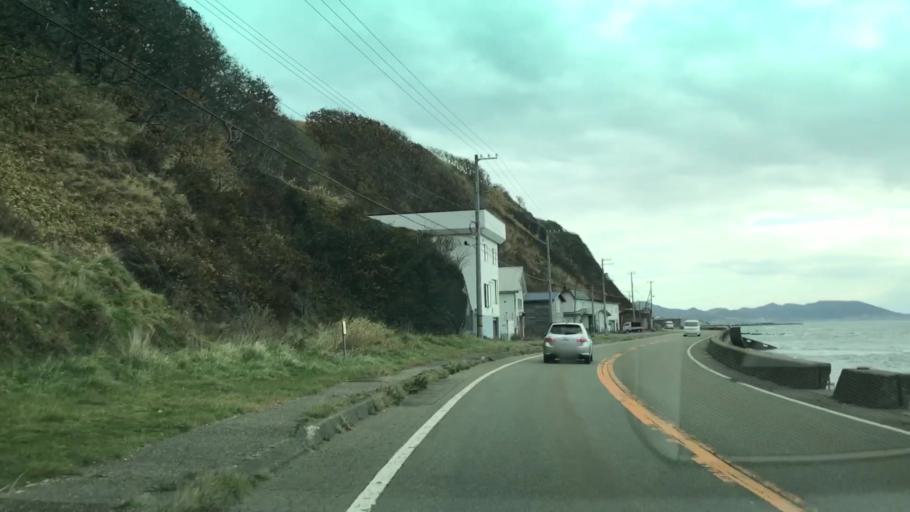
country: JP
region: Hokkaido
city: Shizunai-furukawacho
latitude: 42.0554
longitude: 143.0822
